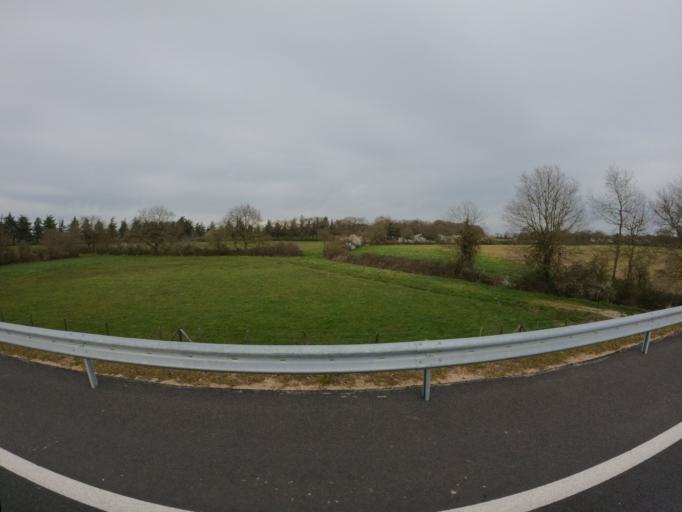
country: FR
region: Pays de la Loire
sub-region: Departement de la Vendee
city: Montaigu
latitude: 46.9856
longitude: -1.2977
